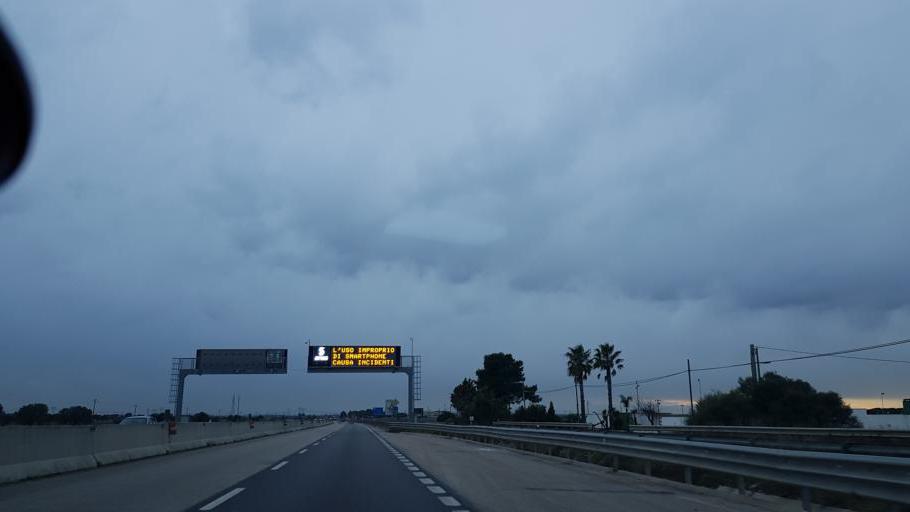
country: IT
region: Apulia
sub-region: Provincia di Brindisi
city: Brindisi
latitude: 40.6149
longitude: 17.9005
